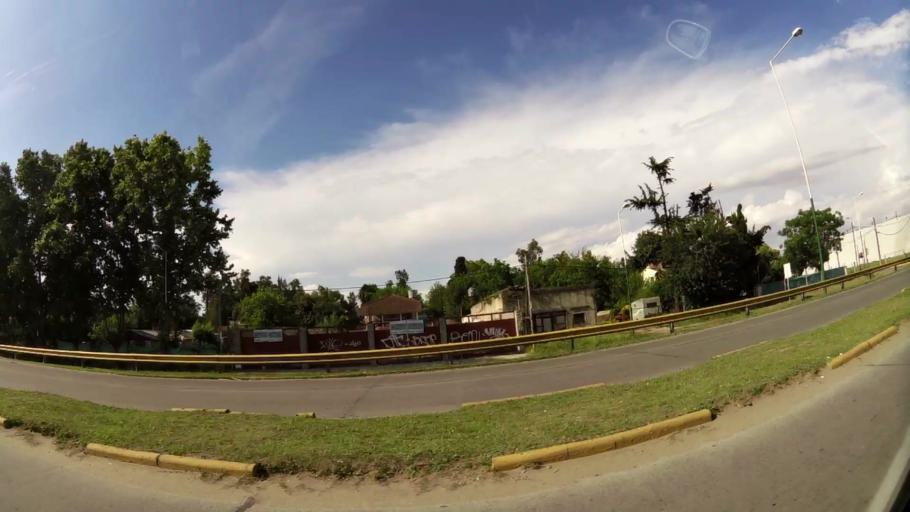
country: AR
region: Buenos Aires
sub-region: Partido de Merlo
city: Merlo
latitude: -34.6609
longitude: -58.7505
